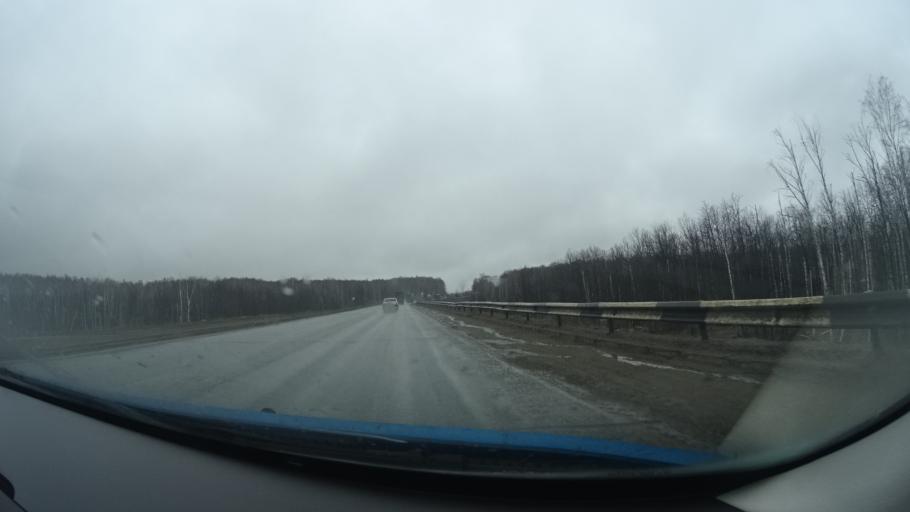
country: RU
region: Bashkortostan
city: Kandry
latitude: 54.5949
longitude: 54.2820
